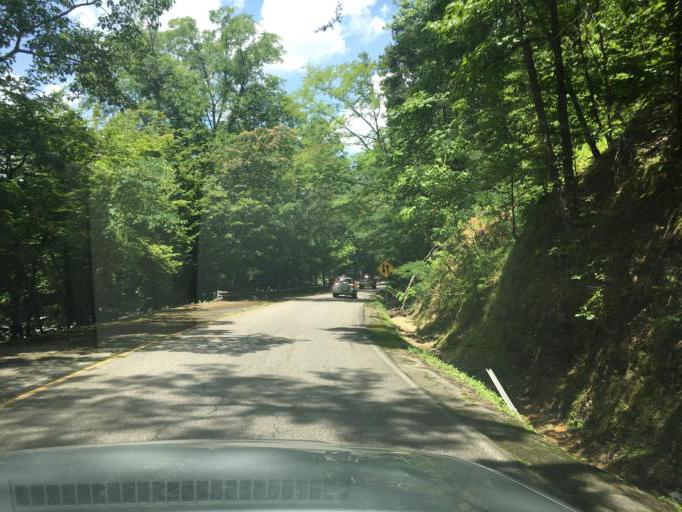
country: US
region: Alabama
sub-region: Jefferson County
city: Mountain Brook
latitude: 33.4734
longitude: -86.7645
